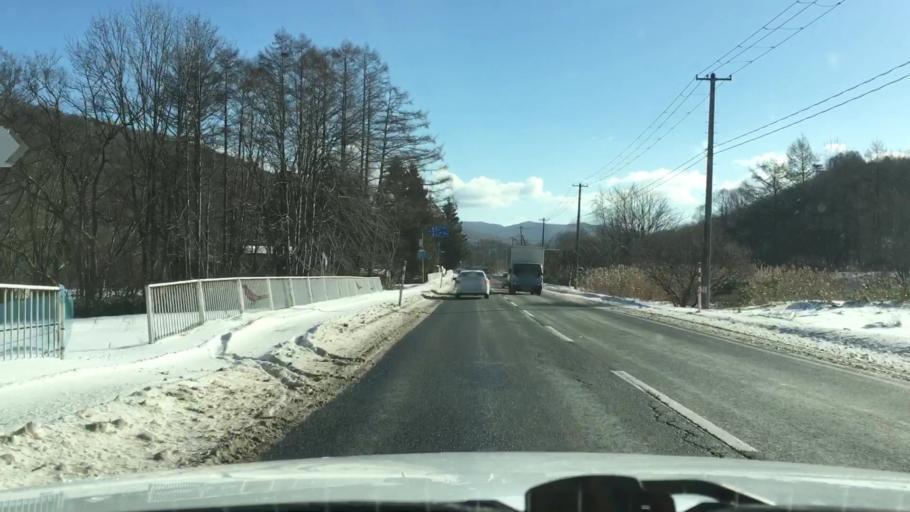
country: JP
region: Iwate
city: Morioka-shi
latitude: 39.6436
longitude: 141.3945
